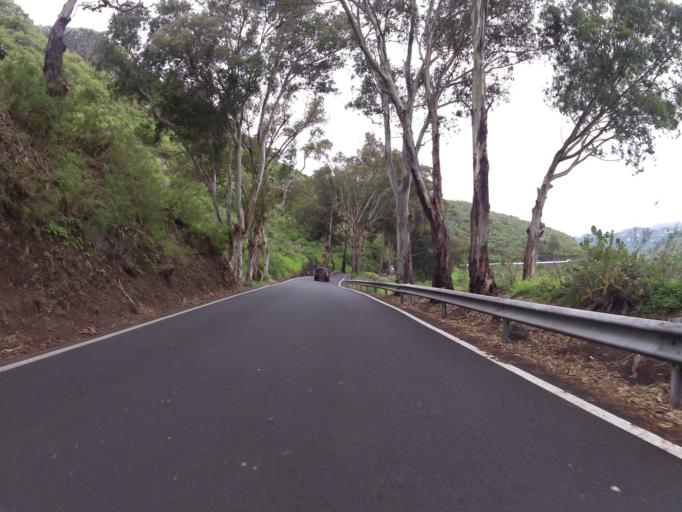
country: ES
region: Canary Islands
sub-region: Provincia de Las Palmas
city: Arucas
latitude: 28.0839
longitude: -15.5103
